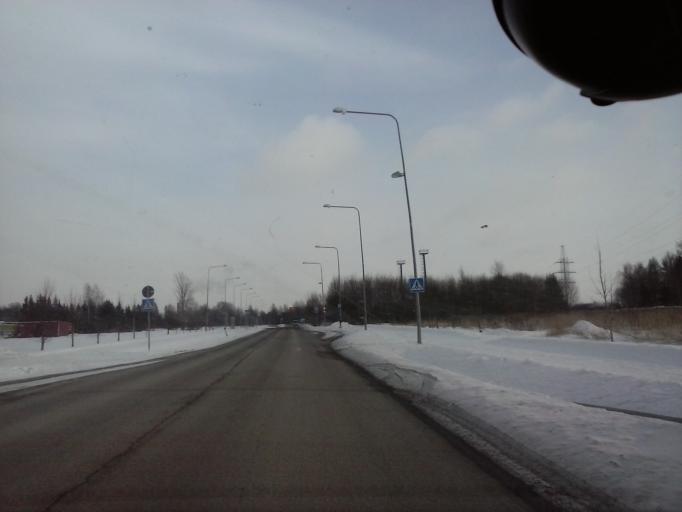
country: EE
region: Tartu
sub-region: Tartu linn
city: Tartu
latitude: 58.3561
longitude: 26.6726
